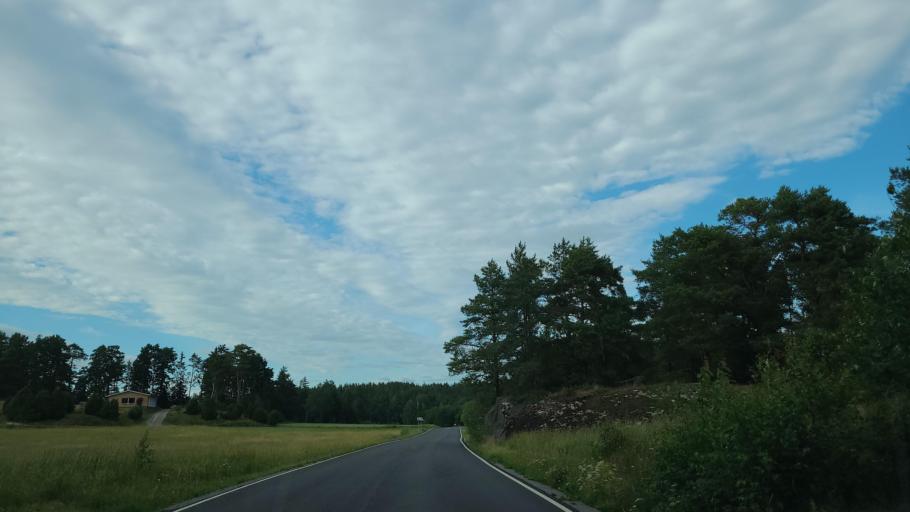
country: FI
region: Varsinais-Suomi
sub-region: Turku
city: Rymaettylae
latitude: 60.3277
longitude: 21.9703
